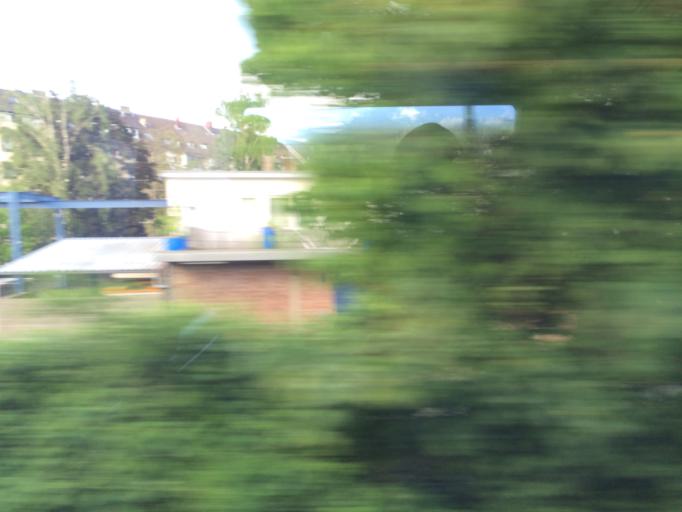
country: DE
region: North Rhine-Westphalia
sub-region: Regierungsbezirk Dusseldorf
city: Dusseldorf
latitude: 51.2105
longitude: 6.7918
